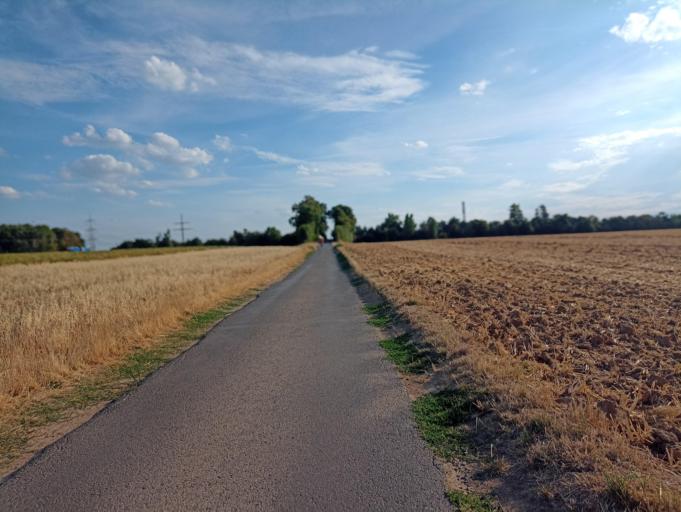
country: DE
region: Hesse
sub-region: Regierungsbezirk Darmstadt
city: Bad Homburg vor der Hoehe
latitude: 50.2048
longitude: 8.6418
